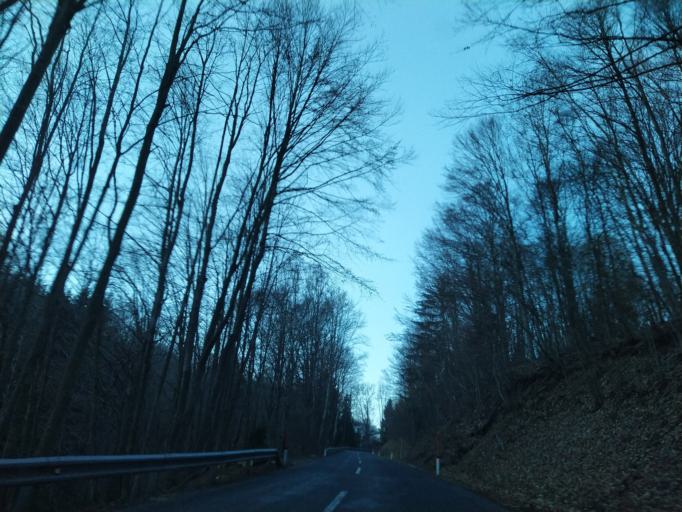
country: AT
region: Upper Austria
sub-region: Politischer Bezirk Urfahr-Umgebung
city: Kirchschlag bei Linz
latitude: 48.3899
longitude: 14.2879
